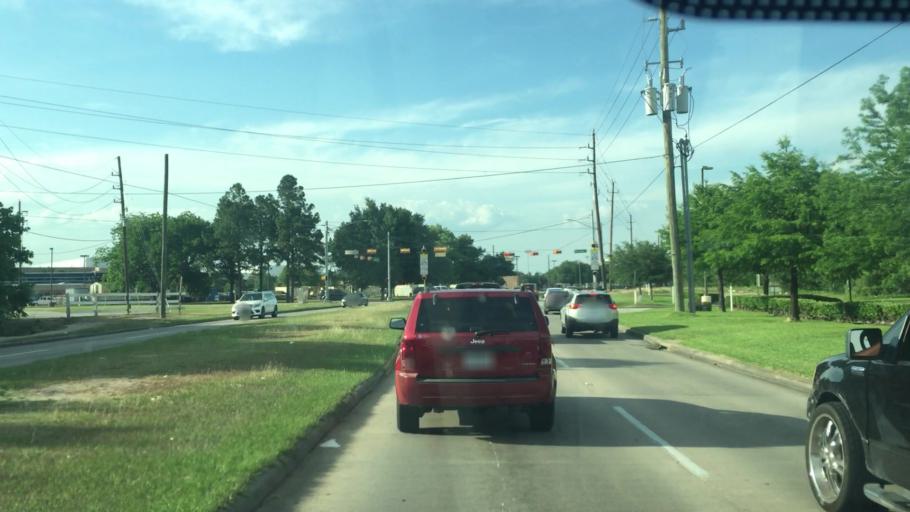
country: US
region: Texas
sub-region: Harris County
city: Hudson
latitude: 29.9619
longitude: -95.4985
